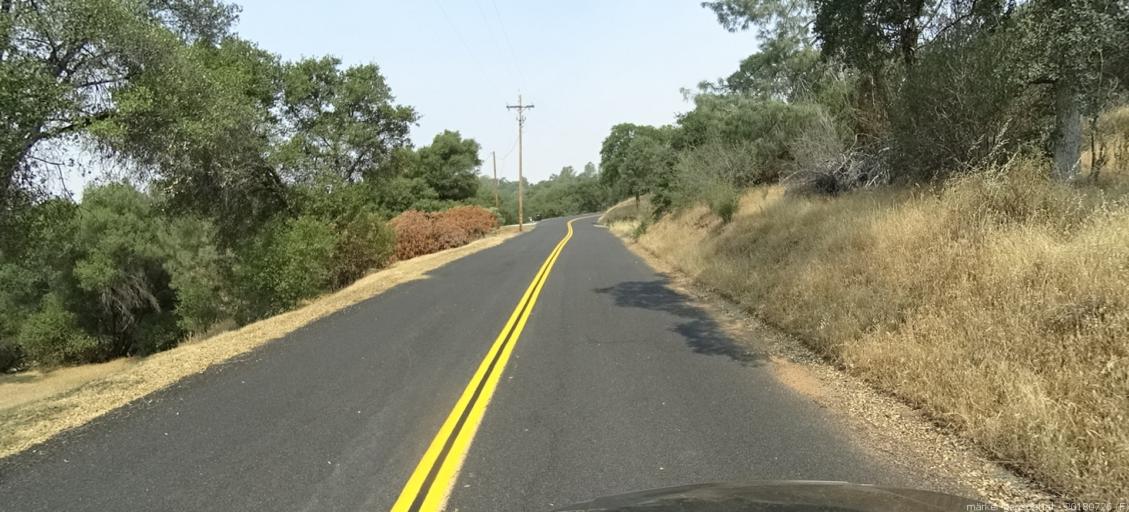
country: US
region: California
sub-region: Madera County
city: Coarsegold
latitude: 37.2490
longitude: -119.6859
